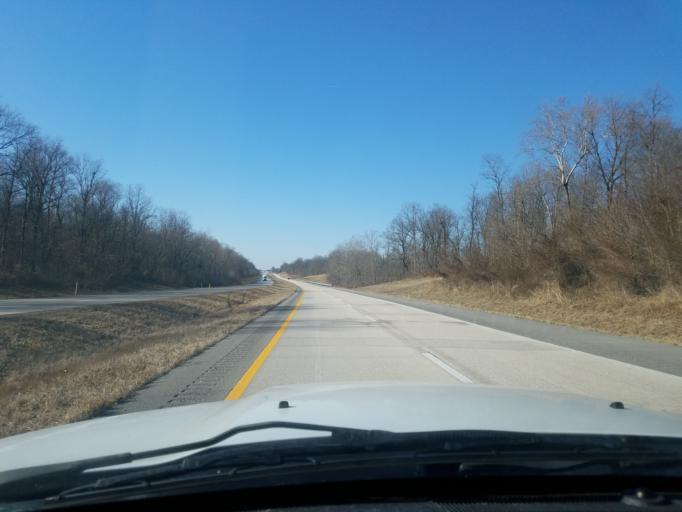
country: US
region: Kentucky
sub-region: Henderson County
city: Henderson
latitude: 37.7743
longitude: -87.4367
